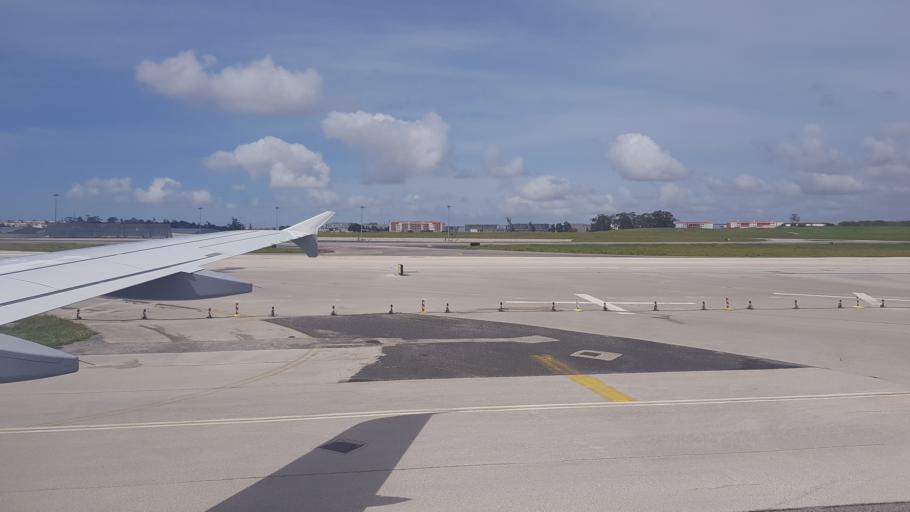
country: PT
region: Lisbon
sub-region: Loures
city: Camarate
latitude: 38.7750
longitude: -9.1330
